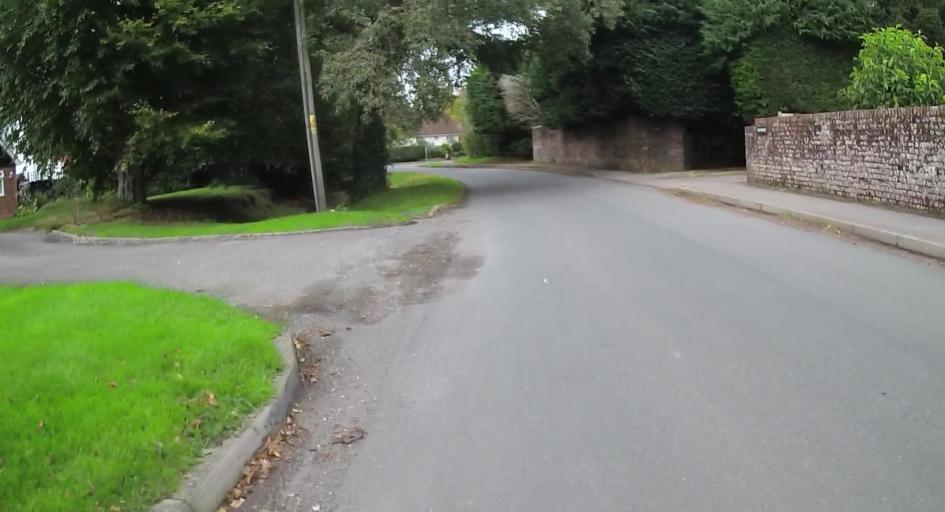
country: GB
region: England
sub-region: Hampshire
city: Alton
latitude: 51.1118
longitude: -0.9853
